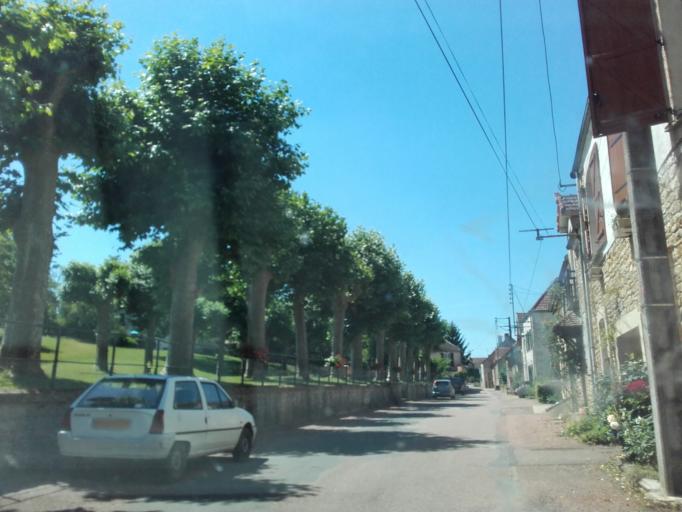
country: FR
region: Bourgogne
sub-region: Departement de Saone-et-Loire
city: Saint-Leger-sur-Dheune
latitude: 46.8946
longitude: 4.6721
